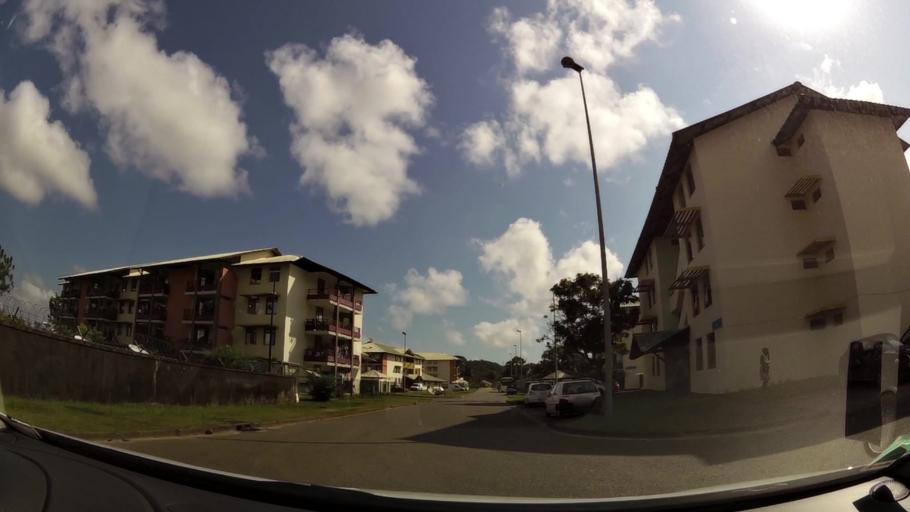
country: GF
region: Guyane
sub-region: Guyane
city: Cayenne
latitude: 4.9345
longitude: -52.3165
